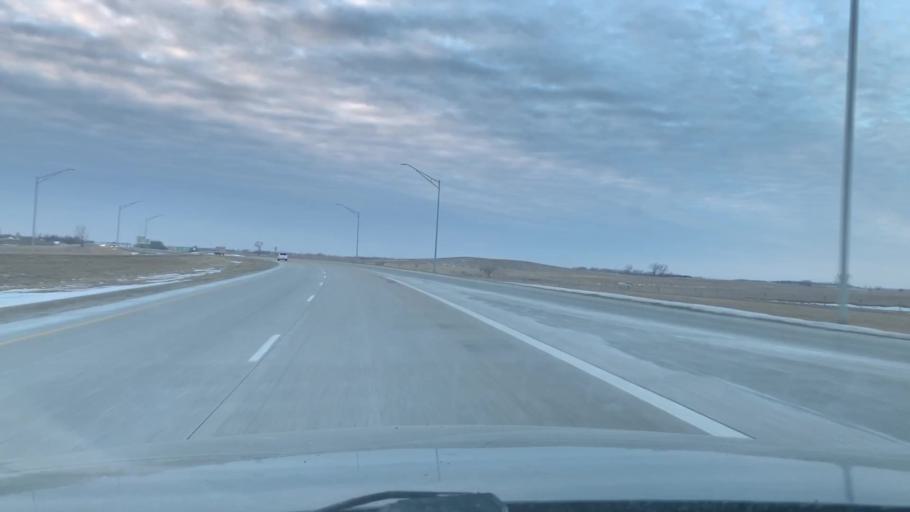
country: US
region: North Dakota
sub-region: Barnes County
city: Valley City
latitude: 46.9197
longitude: -97.6857
